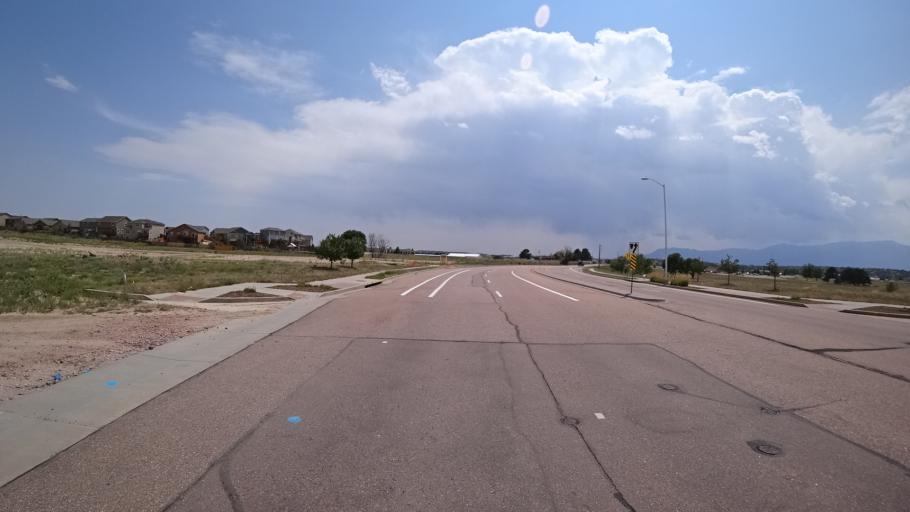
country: US
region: Colorado
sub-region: El Paso County
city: Cimarron Hills
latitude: 38.9307
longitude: -104.7136
